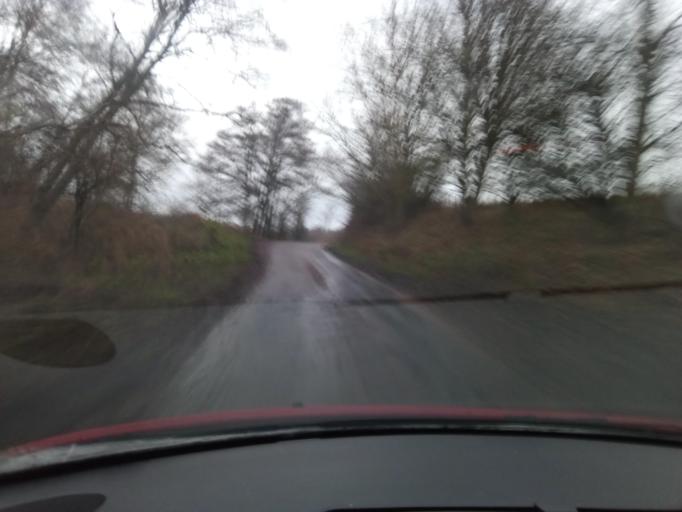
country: GB
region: Scotland
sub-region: The Scottish Borders
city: Kelso
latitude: 55.5458
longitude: -2.4347
